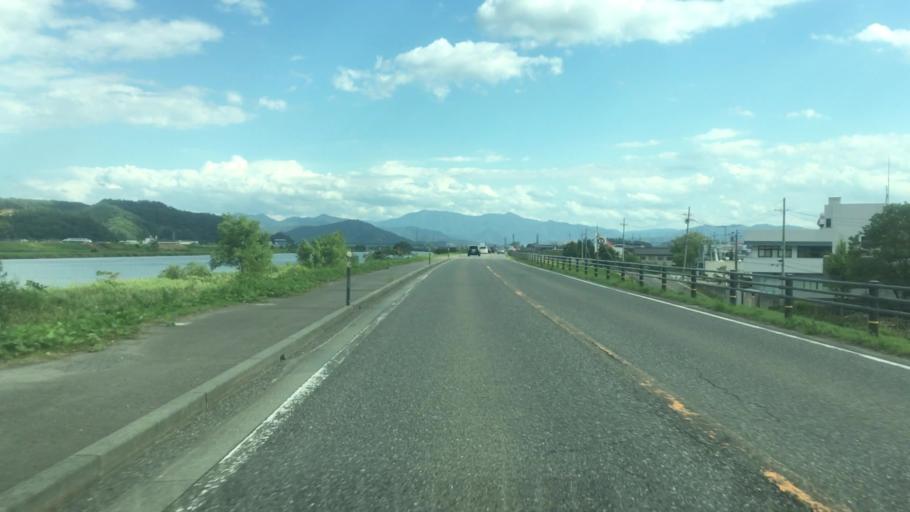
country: JP
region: Hyogo
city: Toyooka
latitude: 35.5719
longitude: 134.8077
